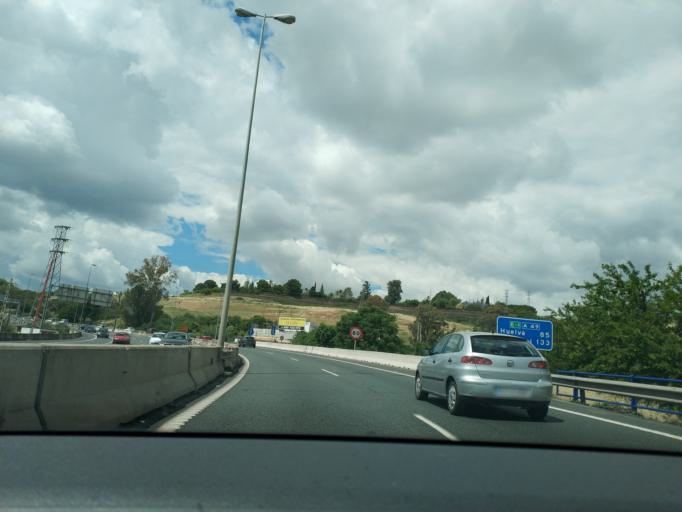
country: ES
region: Andalusia
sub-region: Provincia de Sevilla
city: Camas
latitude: 37.3897
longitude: -6.0329
